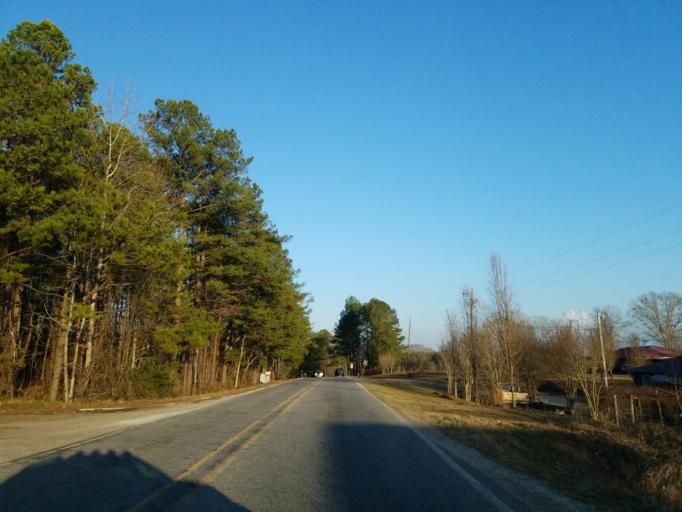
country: US
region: Mississippi
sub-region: Clarke County
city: Stonewall
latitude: 32.1642
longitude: -88.8644
